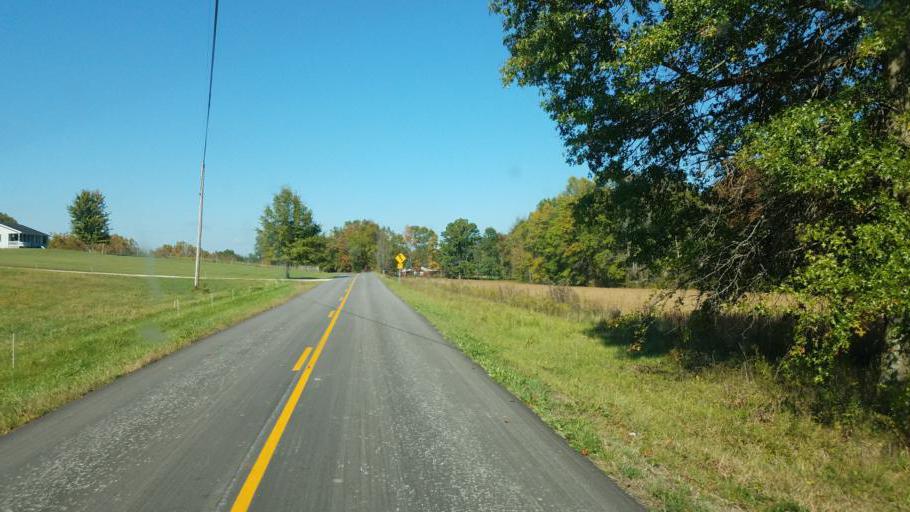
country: US
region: Kentucky
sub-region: Fleming County
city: Flemingsburg
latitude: 38.4559
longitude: -83.5832
